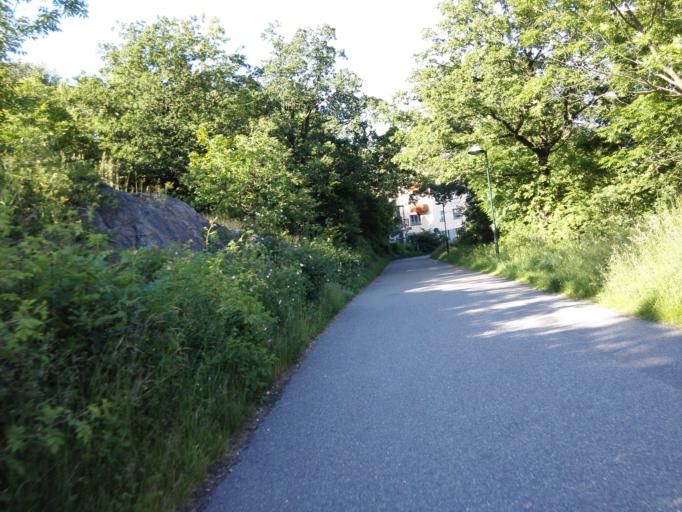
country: SE
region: Stockholm
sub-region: Stockholms Kommun
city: Arsta
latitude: 59.2996
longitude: 18.0107
